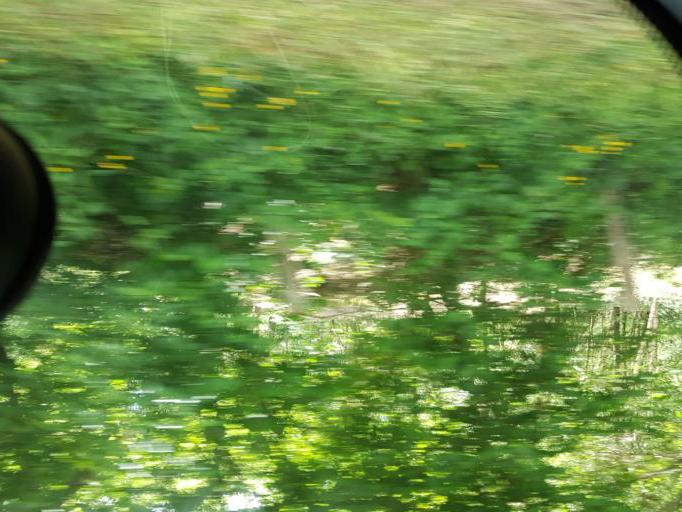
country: FR
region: Bourgogne
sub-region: Departement de la Cote-d'Or
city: Saulieu
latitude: 47.1745
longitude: 4.1221
